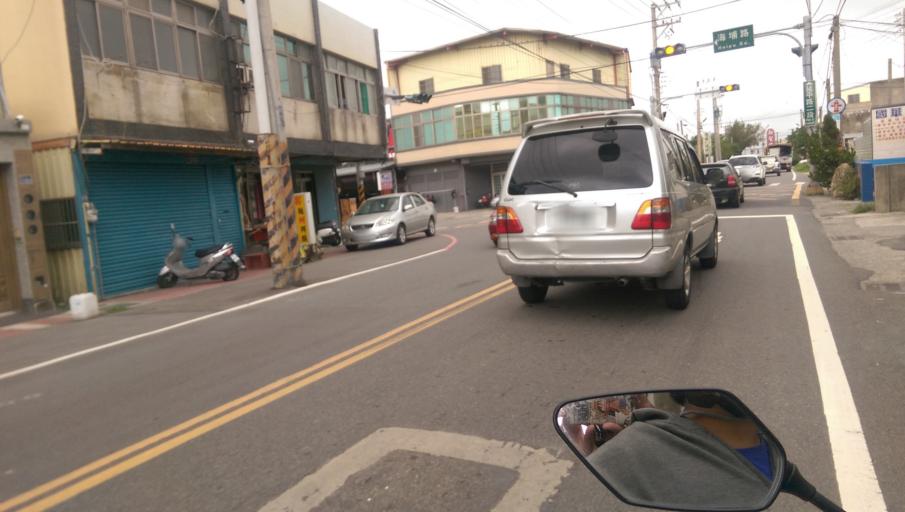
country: TW
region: Taiwan
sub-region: Hsinchu
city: Hsinchu
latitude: 24.8178
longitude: 120.9291
